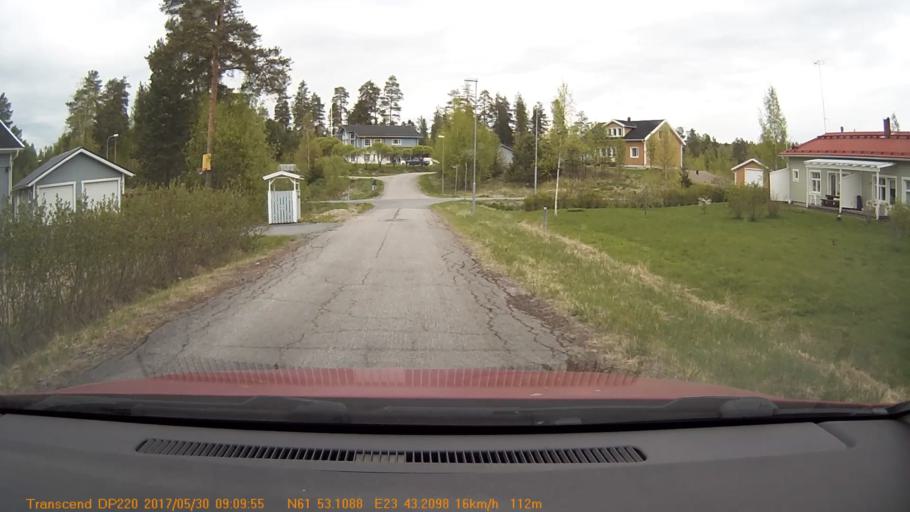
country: FI
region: Pirkanmaa
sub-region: Tampere
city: Kuru
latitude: 61.8852
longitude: 23.7202
